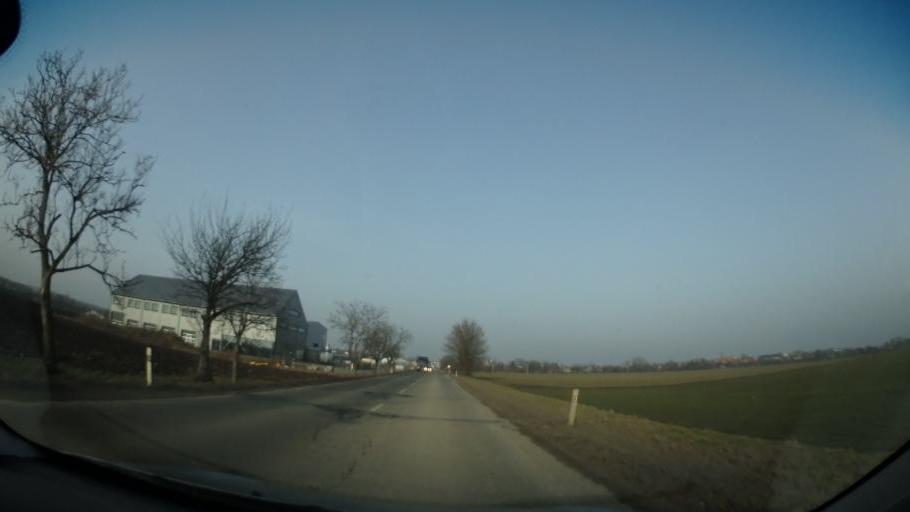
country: CZ
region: South Moravian
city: Rajhrad
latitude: 49.0827
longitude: 16.5873
